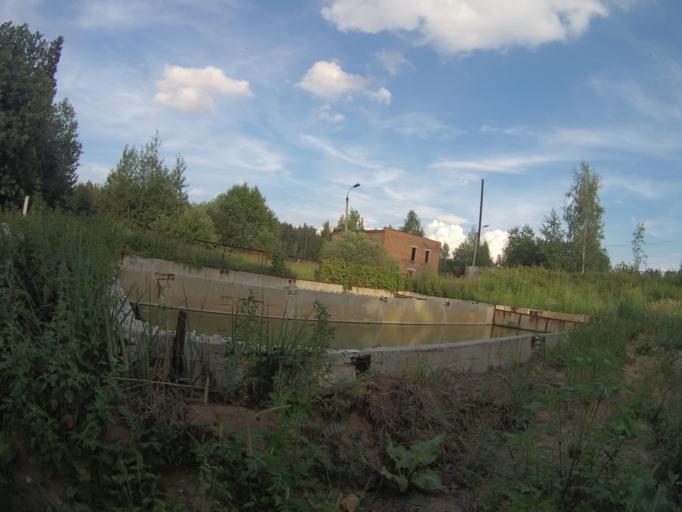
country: RU
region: Vladimir
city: Vorsha
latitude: 56.0040
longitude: 40.0666
